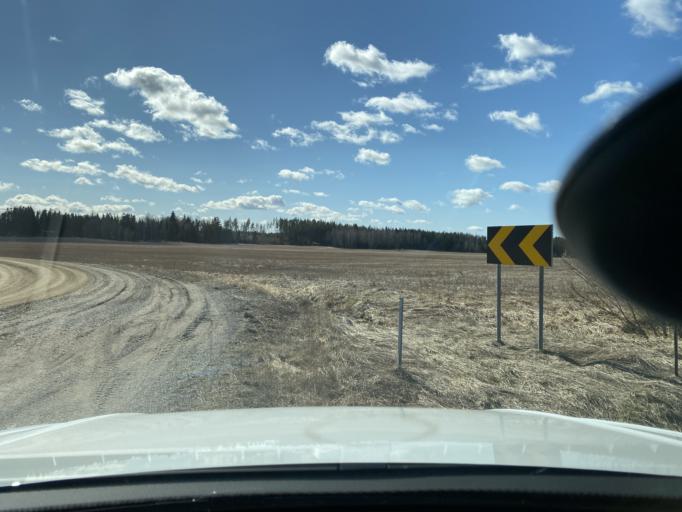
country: FI
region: Pirkanmaa
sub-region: Lounais-Pirkanmaa
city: Punkalaidun
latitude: 61.0528
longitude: 23.1863
